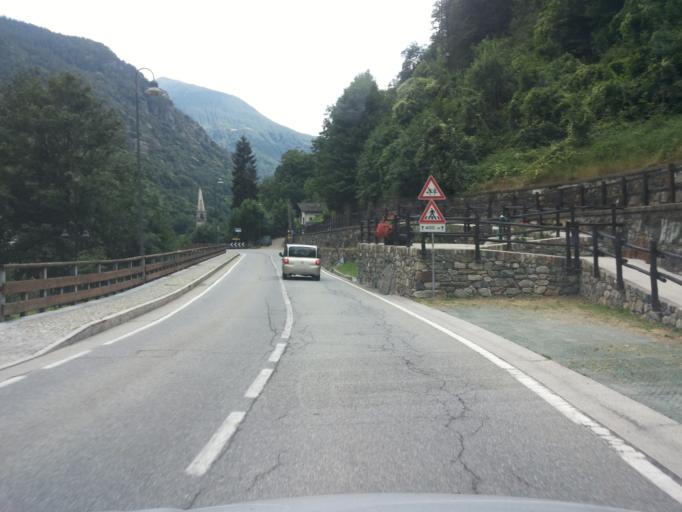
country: IT
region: Aosta Valley
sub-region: Valle d'Aosta
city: Fontainemore
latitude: 45.6503
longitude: 7.8599
